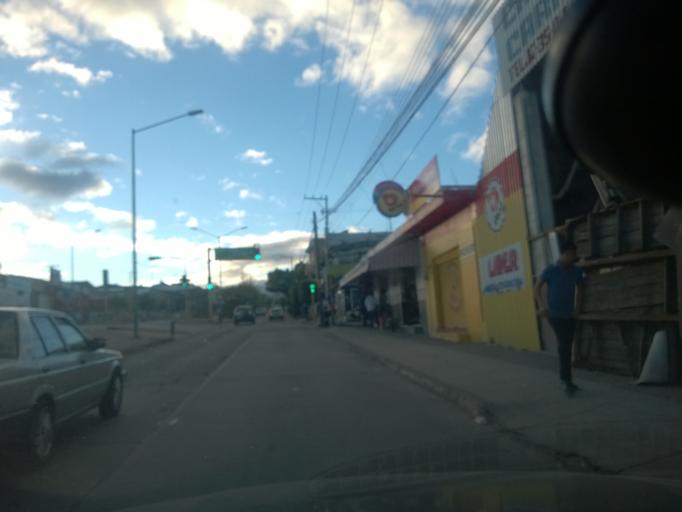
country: MX
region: Guanajuato
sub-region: Leon
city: La Ermita
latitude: 21.1325
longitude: -101.7112
